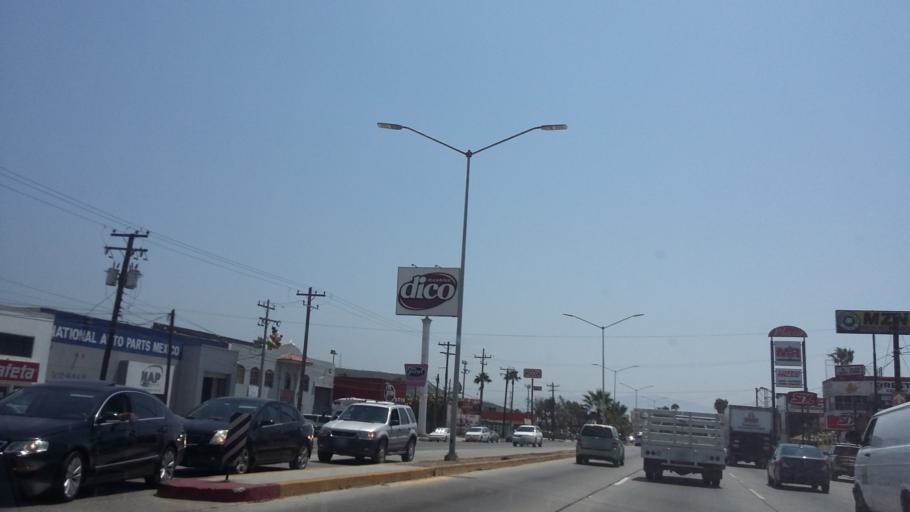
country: MX
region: Baja California
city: Ensenada
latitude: 31.8352
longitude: -116.6017
